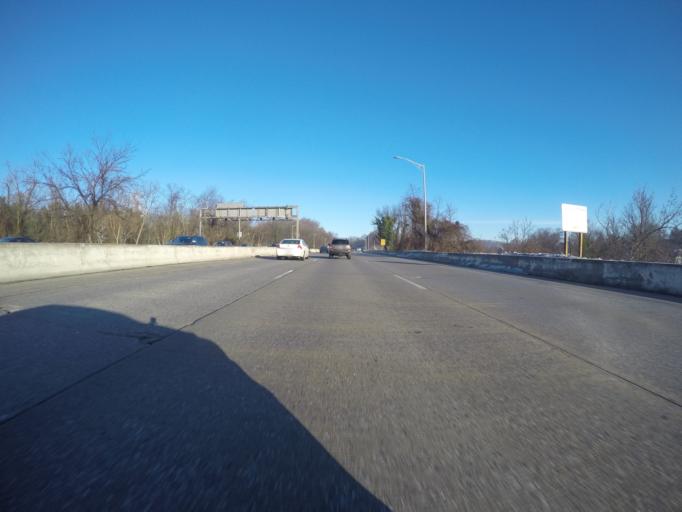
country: US
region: Maryland
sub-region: Baltimore County
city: Lutherville
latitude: 39.3688
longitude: -76.6514
